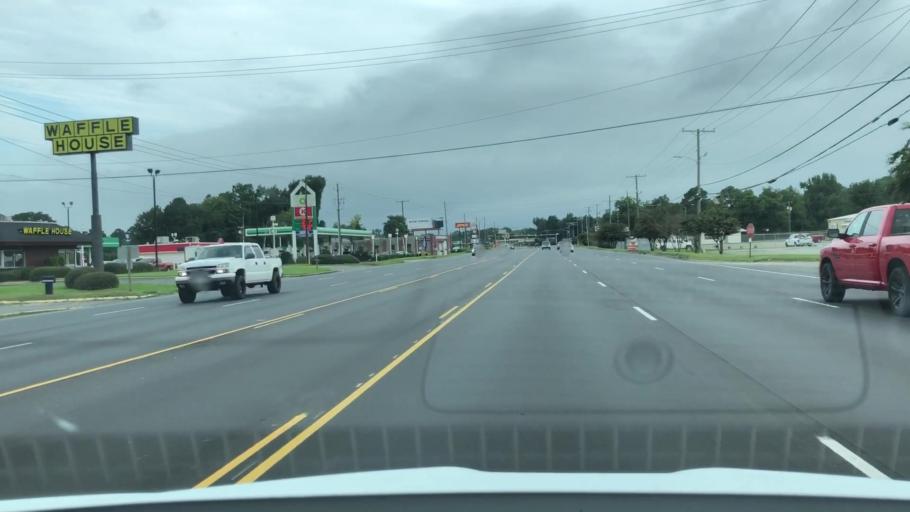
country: US
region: North Carolina
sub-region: Lenoir County
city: Kinston
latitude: 35.2389
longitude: -77.5754
